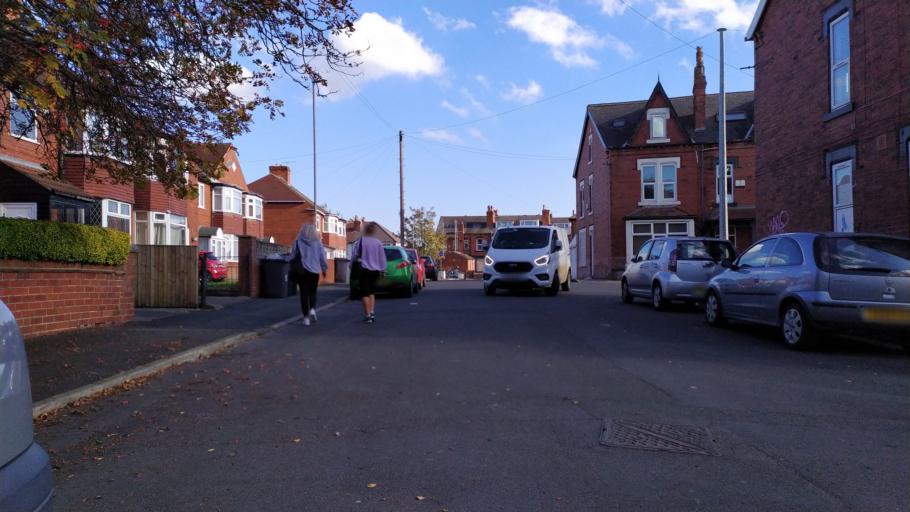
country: GB
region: England
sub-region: City and Borough of Leeds
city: Leeds
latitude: 53.8216
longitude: -1.5857
